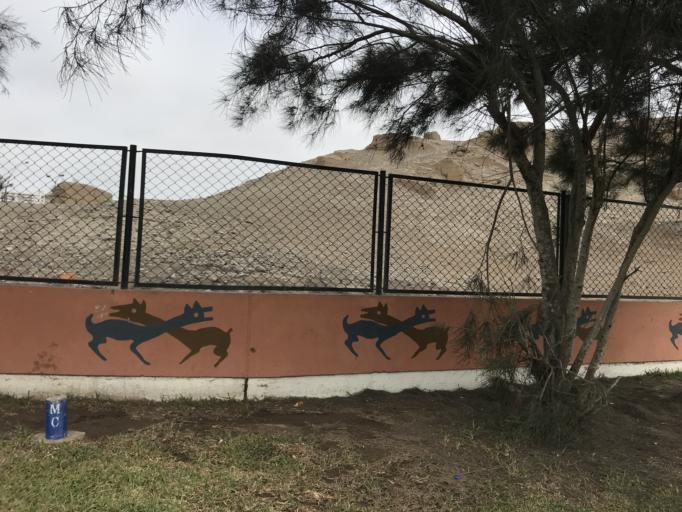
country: PE
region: Callao
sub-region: Callao
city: Callao
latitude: -12.0707
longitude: -77.0831
